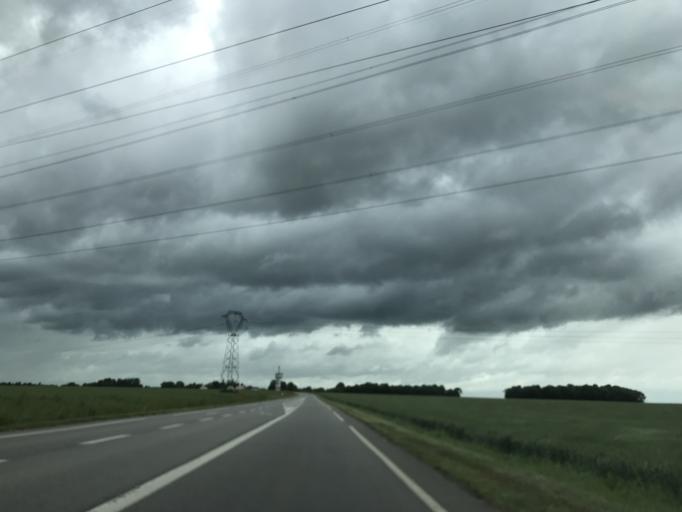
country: FR
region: Haute-Normandie
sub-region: Departement de l'Eure
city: La Couture-Boussey
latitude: 48.8942
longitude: 1.4222
